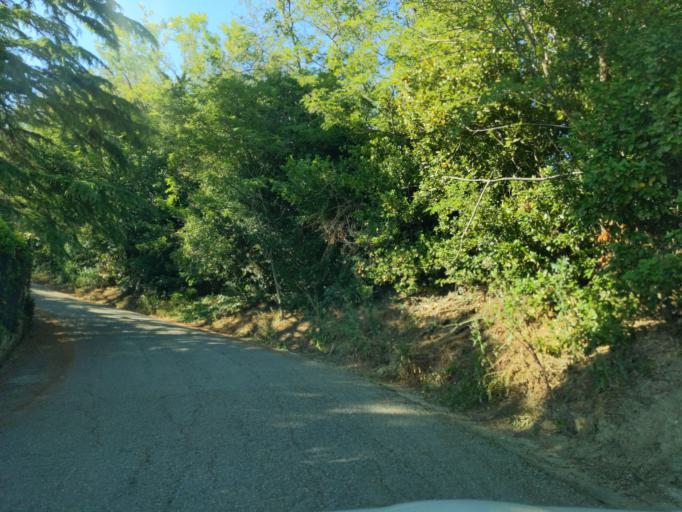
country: IT
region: The Marches
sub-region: Provincia di Pesaro e Urbino
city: Cuccurano
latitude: 43.7996
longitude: 12.9606
